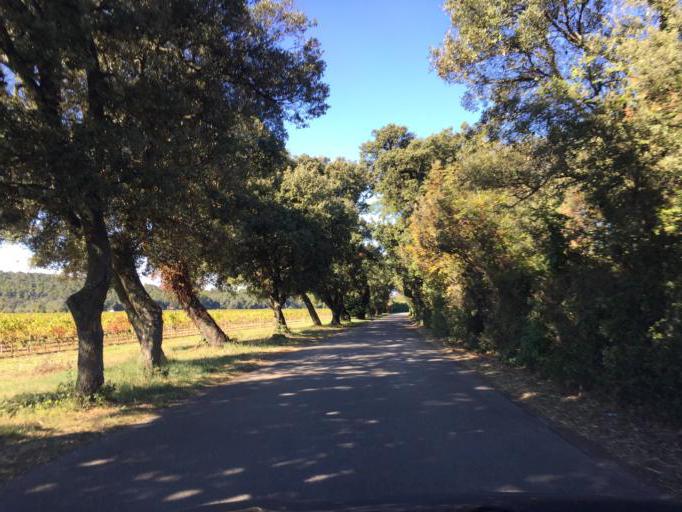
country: FR
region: Provence-Alpes-Cote d'Azur
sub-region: Departement du Vaucluse
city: Piolenc
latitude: 44.1658
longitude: 4.7908
